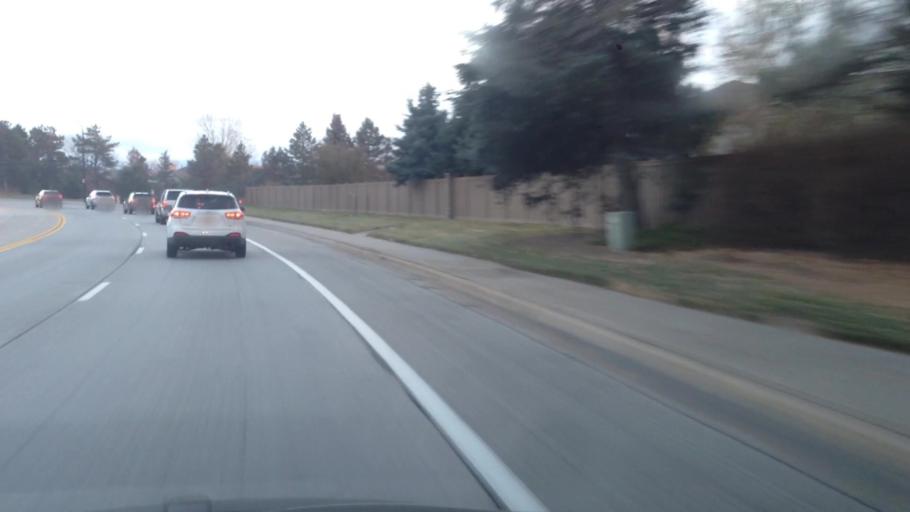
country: US
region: Colorado
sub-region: Douglas County
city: Carriage Club
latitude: 39.5371
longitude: -104.9073
